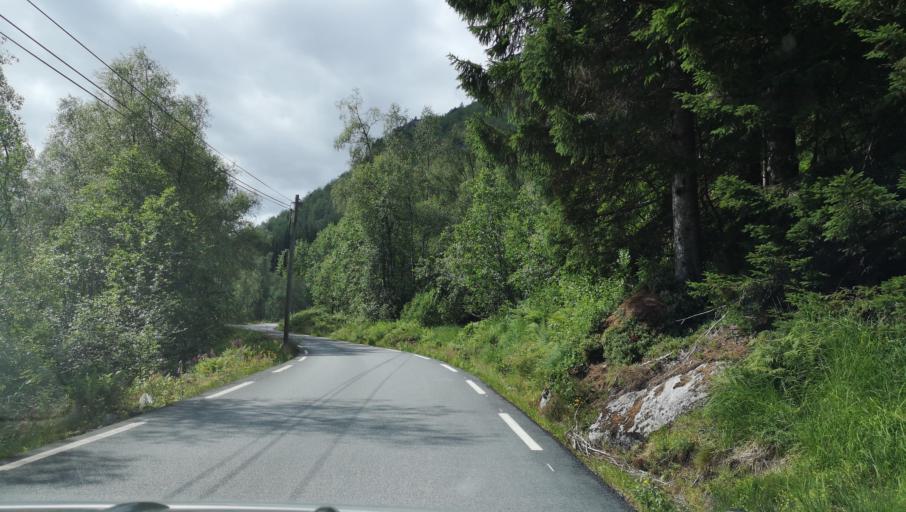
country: NO
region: Hordaland
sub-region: Modalen
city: Mo
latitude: 60.7863
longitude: 5.9389
